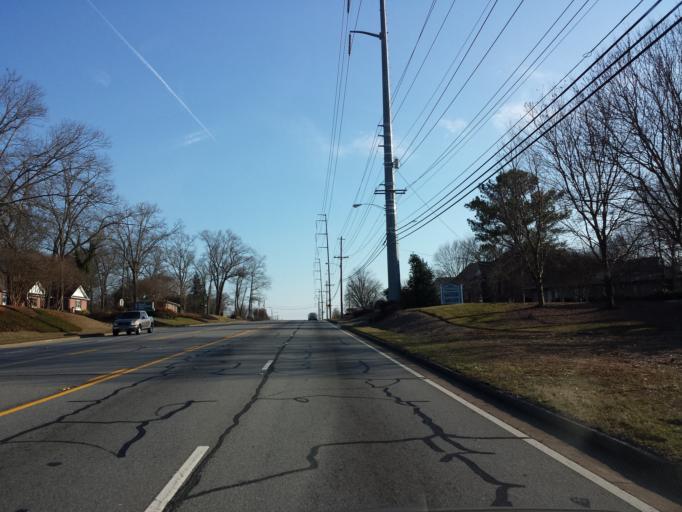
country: US
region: Georgia
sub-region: Cherokee County
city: Woodstock
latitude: 34.0434
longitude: -84.5295
